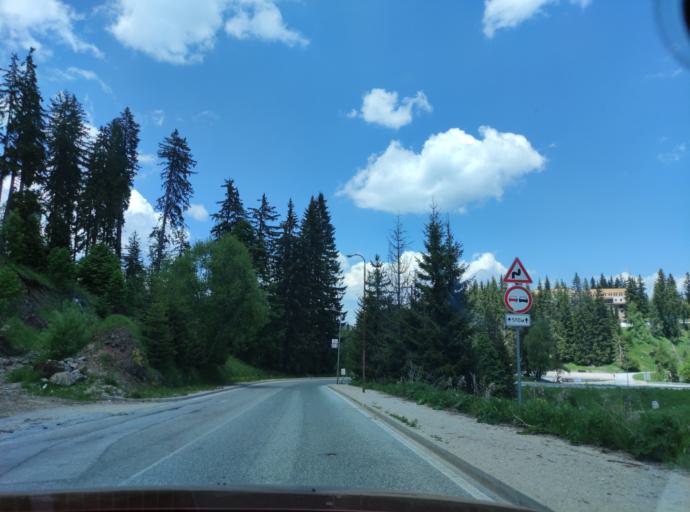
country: BG
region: Smolyan
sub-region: Obshtina Smolyan
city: Smolyan
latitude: 41.6493
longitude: 24.6983
